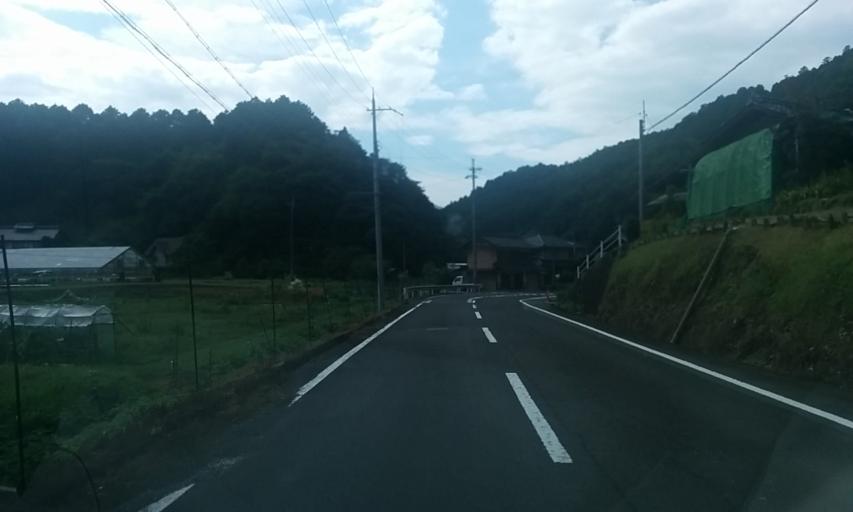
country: JP
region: Kyoto
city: Fukuchiyama
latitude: 35.3739
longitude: 135.1555
